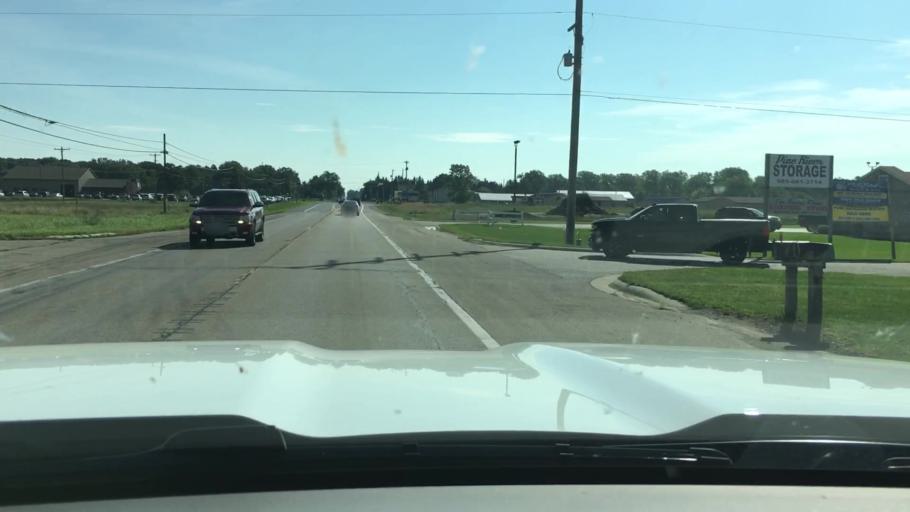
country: US
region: Michigan
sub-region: Gratiot County
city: Saint Louis
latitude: 43.4079
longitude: -84.6371
